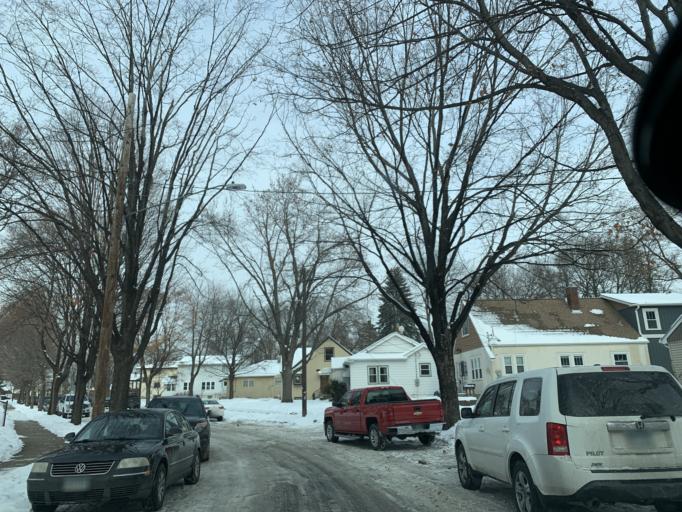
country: US
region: Minnesota
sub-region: Dakota County
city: Mendota Heights
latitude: 44.9060
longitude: -93.2025
